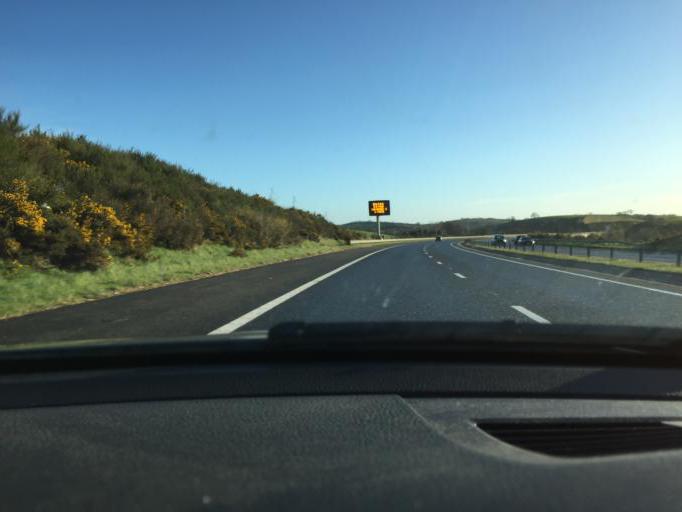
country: GB
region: Northern Ireland
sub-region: Newry and Mourne District
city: Newry
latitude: 54.2091
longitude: -6.3591
